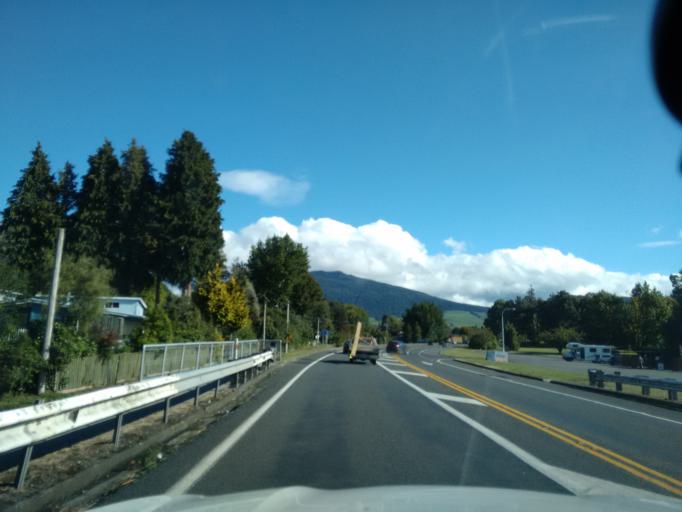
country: NZ
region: Waikato
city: Turangi
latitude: -38.9867
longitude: 175.8183
